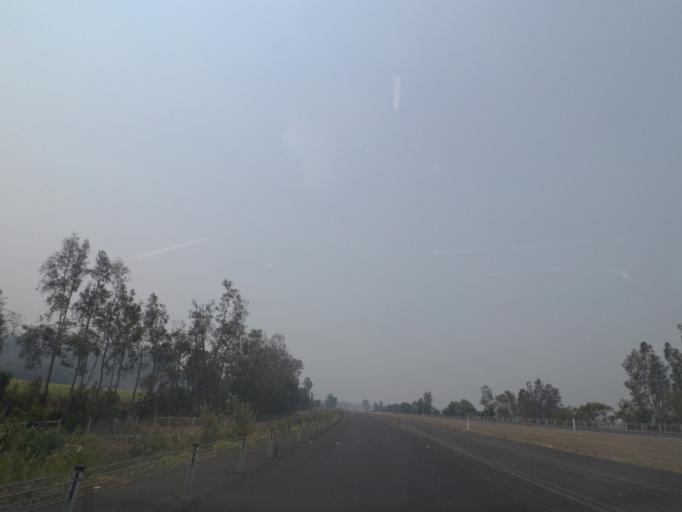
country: AU
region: New South Wales
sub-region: Ballina
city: Ballina
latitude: -28.8781
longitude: 153.4876
